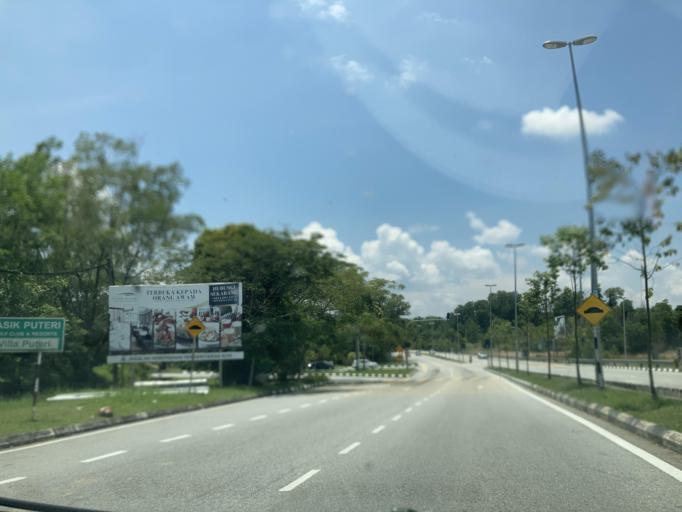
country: MY
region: Selangor
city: Batu Arang
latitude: 3.2905
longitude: 101.4770
